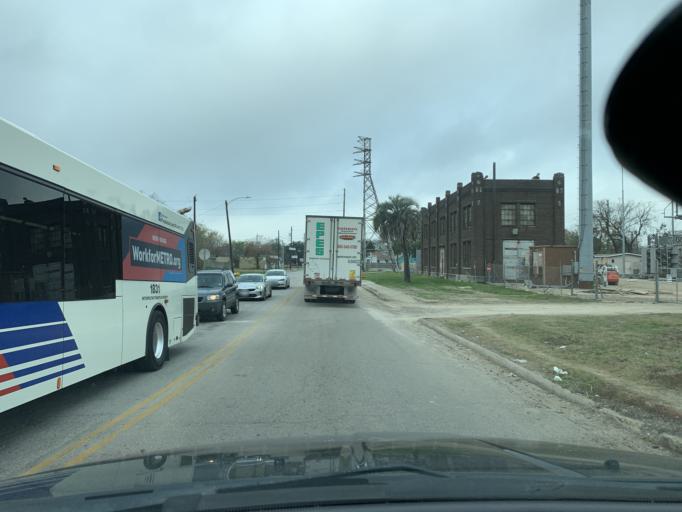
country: US
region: Texas
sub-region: Harris County
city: Houston
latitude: 29.7835
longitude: -95.3490
